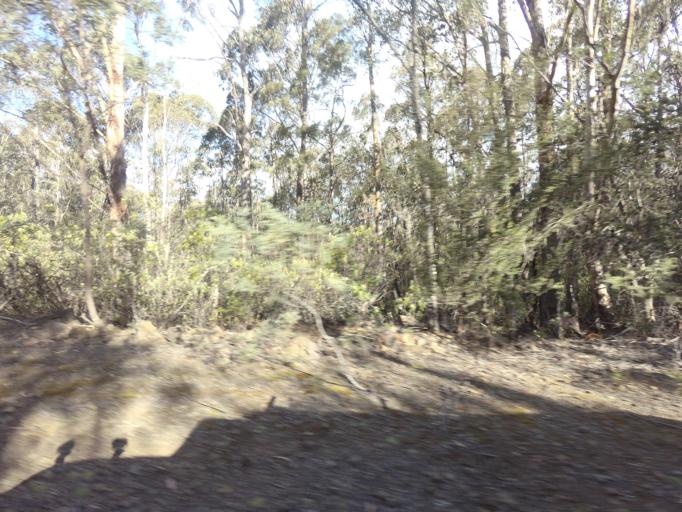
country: AU
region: Tasmania
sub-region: Break O'Day
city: St Helens
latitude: -41.8459
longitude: 148.0586
